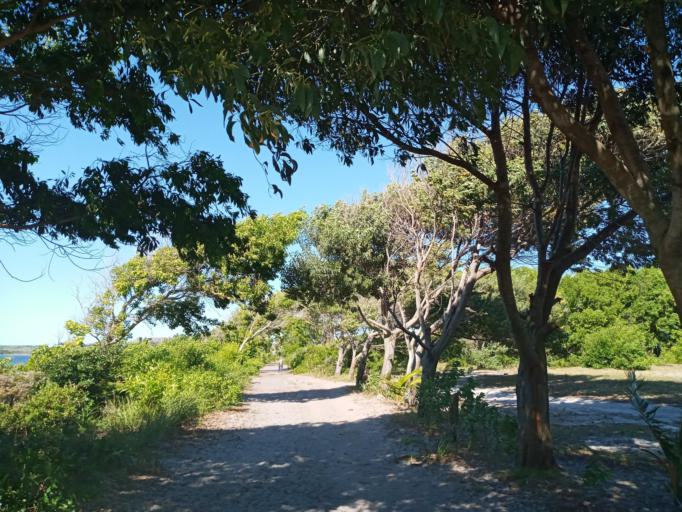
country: MG
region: Anosy
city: Fort Dauphin
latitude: -24.9066
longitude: 47.1026
